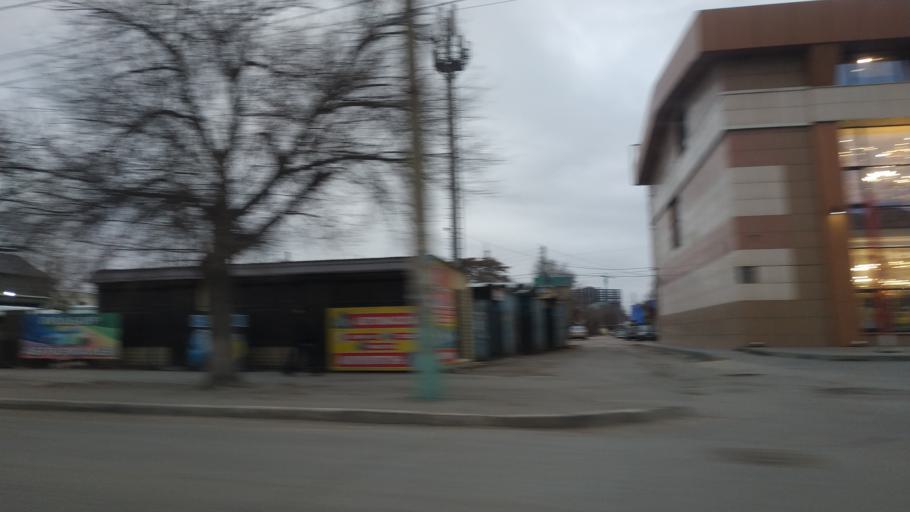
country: RU
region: Astrakhan
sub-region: Gorod Astrakhan'
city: Astrakhan'
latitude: 46.3325
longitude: 48.0121
